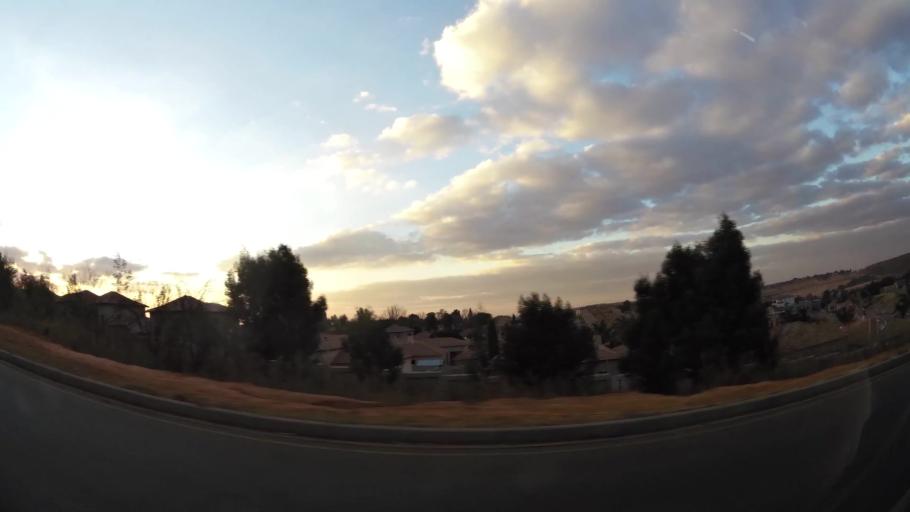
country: ZA
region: Gauteng
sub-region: West Rand District Municipality
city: Krugersdorp
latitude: -26.0760
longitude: 27.7911
